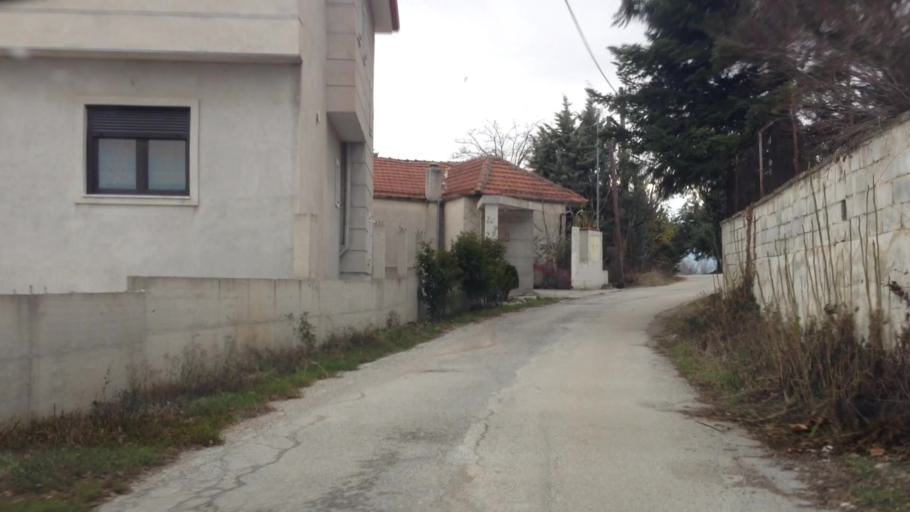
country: GR
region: West Macedonia
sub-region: Nomos Kozanis
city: Kozani
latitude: 40.2934
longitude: 21.7694
